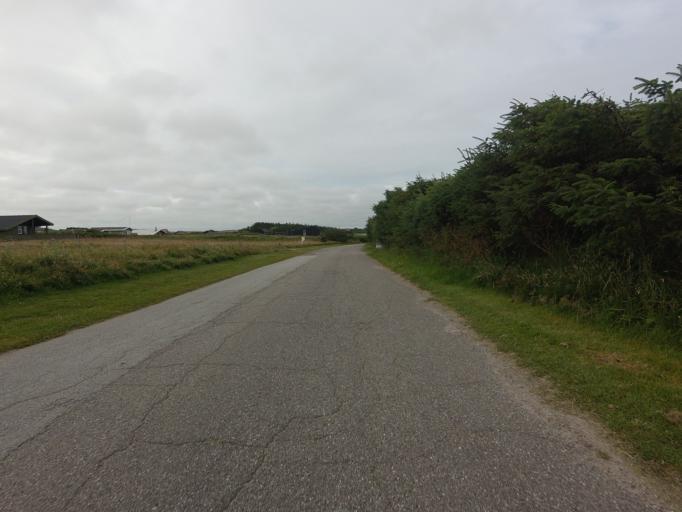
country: DK
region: North Denmark
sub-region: Jammerbugt Kommune
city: Pandrup
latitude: 57.3889
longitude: 9.7286
